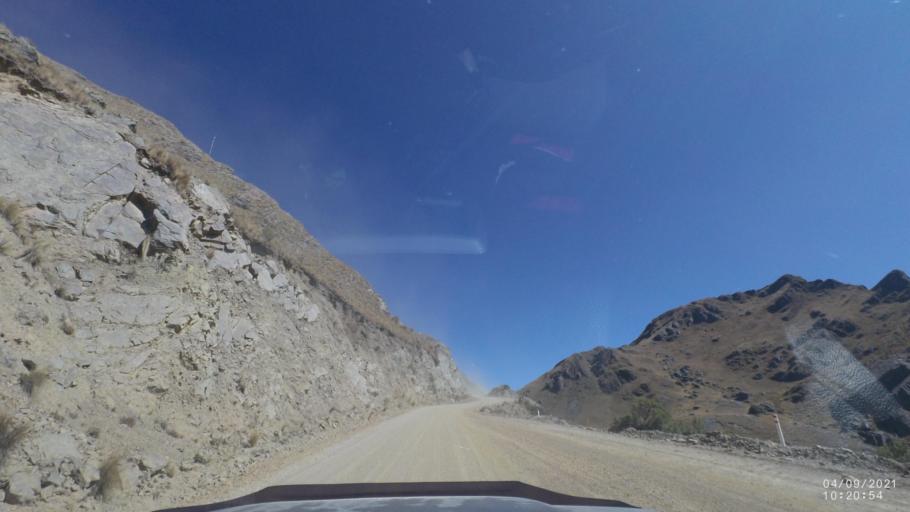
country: BO
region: Cochabamba
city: Sipe Sipe
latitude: -17.3130
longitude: -66.4297
